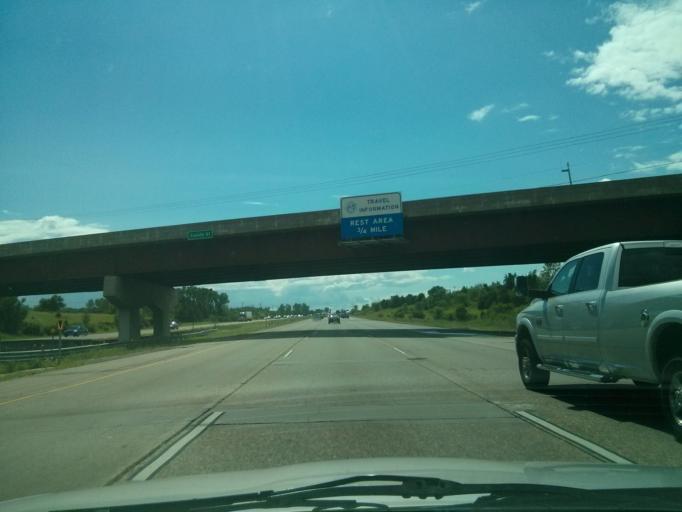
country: US
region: Minnesota
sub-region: Washington County
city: Lakeland
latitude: 44.9551
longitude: -92.7963
